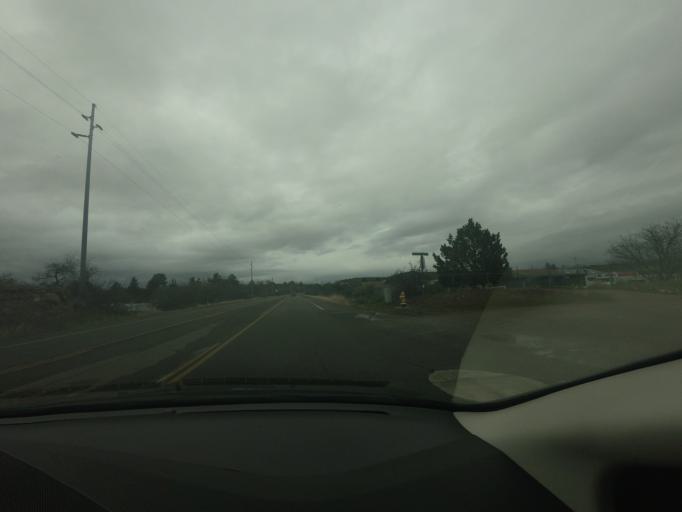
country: US
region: Arizona
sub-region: Yavapai County
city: Lake Montezuma
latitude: 34.6475
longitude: -111.7852
